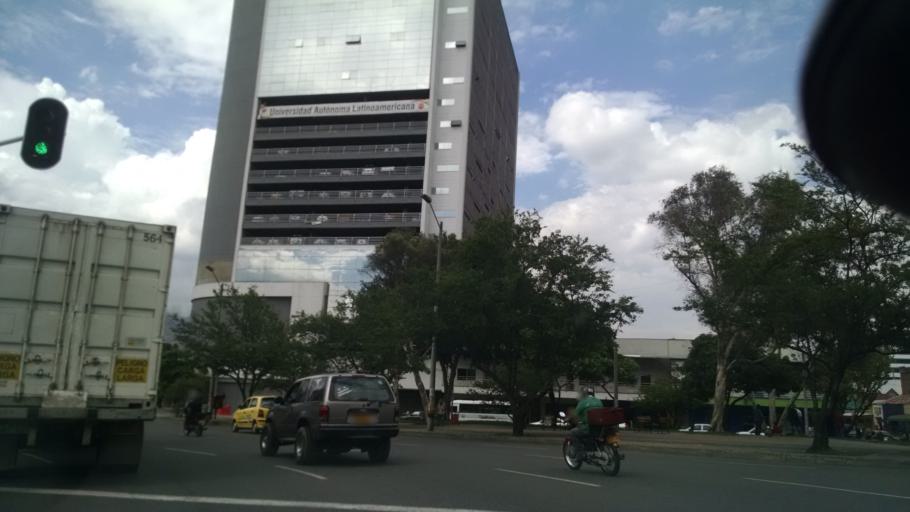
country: CO
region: Antioquia
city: Medellin
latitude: 6.2462
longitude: -75.5747
